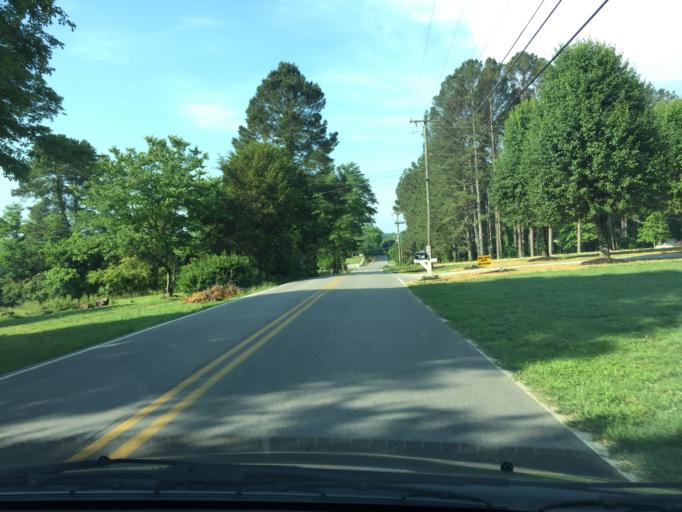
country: US
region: Tennessee
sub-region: Hamilton County
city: Collegedale
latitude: 35.0603
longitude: -85.0146
